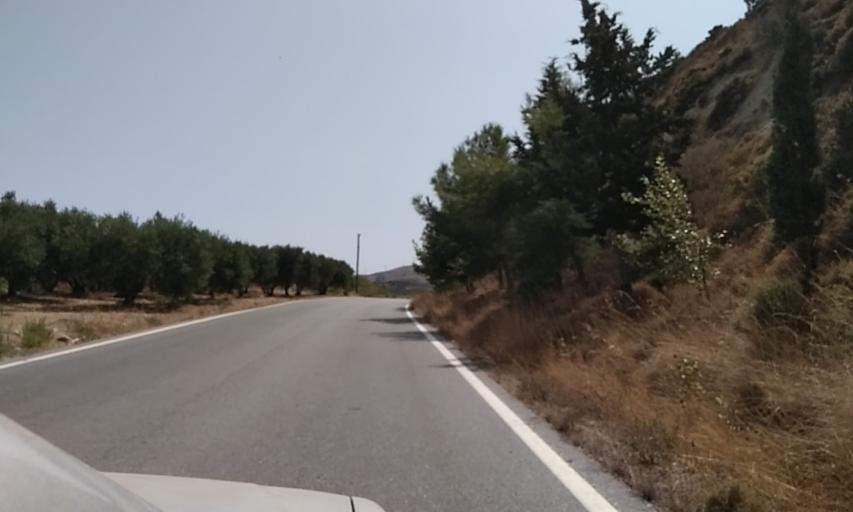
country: GR
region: Crete
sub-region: Nomos Lasithiou
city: Siteia
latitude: 35.1085
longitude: 26.0583
